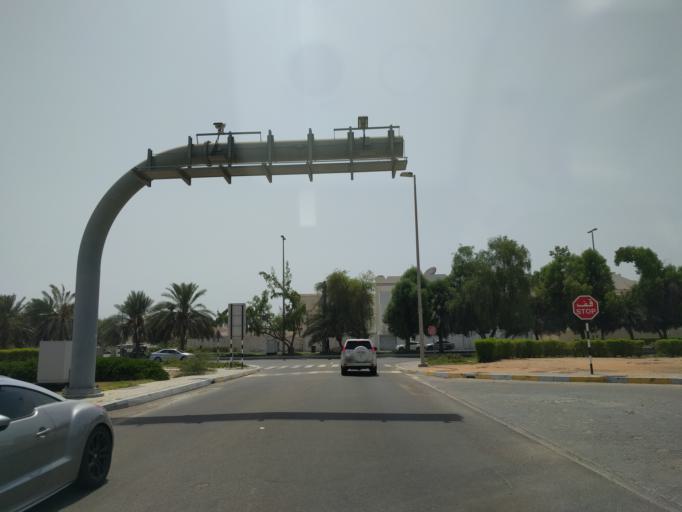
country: AE
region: Abu Dhabi
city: Abu Dhabi
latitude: 24.4258
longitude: 54.4289
